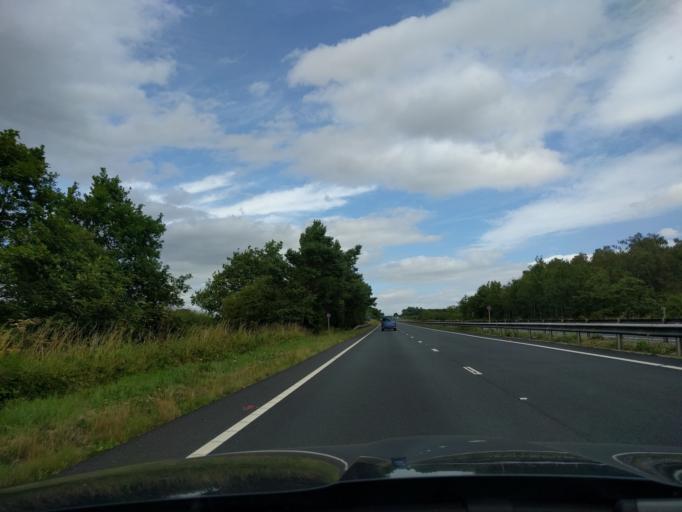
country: GB
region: England
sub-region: Northumberland
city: Felton
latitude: 55.3063
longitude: -1.7259
